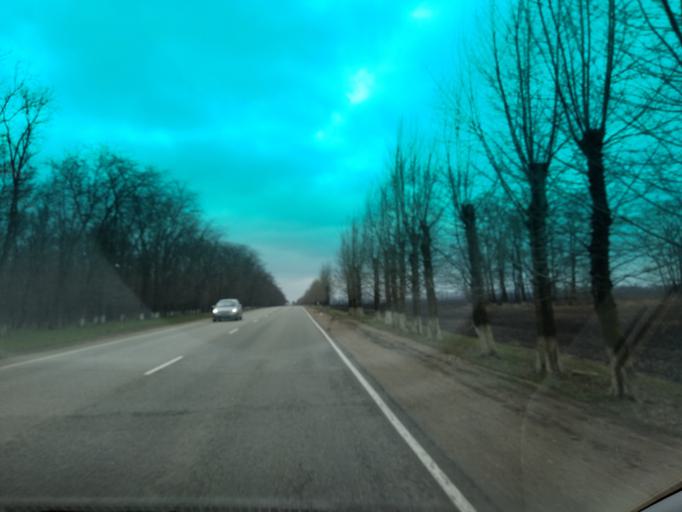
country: RU
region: Krasnodarskiy
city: Novorozhdestvenskaya
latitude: 45.7955
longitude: 39.9787
